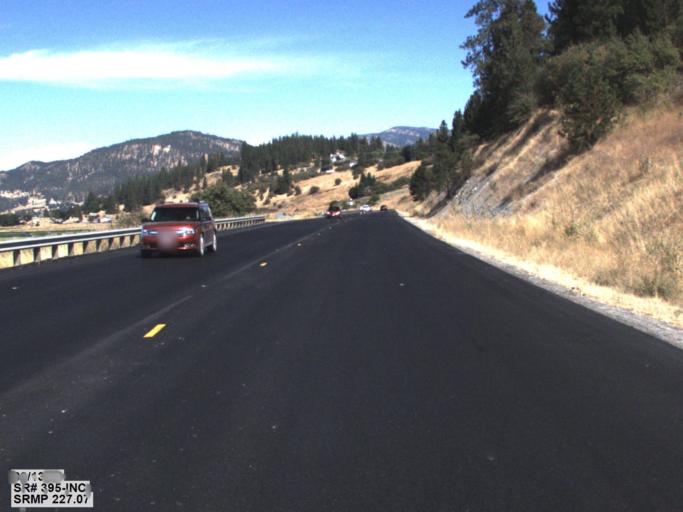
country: US
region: Washington
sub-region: Stevens County
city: Colville
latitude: 48.5095
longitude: -117.9014
